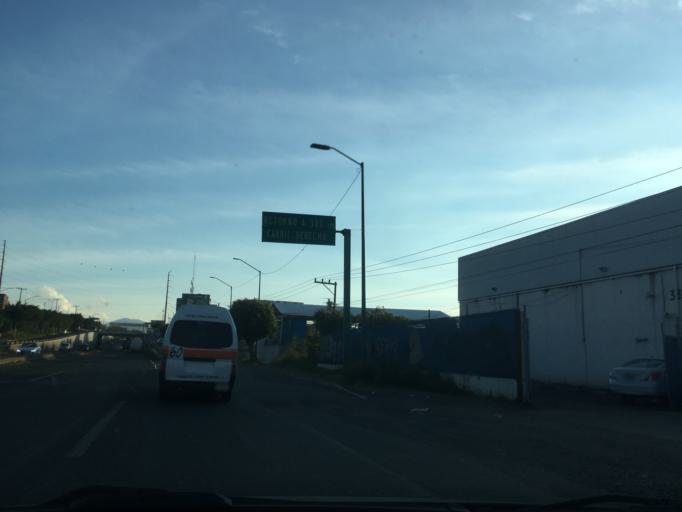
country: MX
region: Michoacan
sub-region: Tarimbaro
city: Fraccionamiento Privadas del Sol
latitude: 19.7351
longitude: -101.1828
